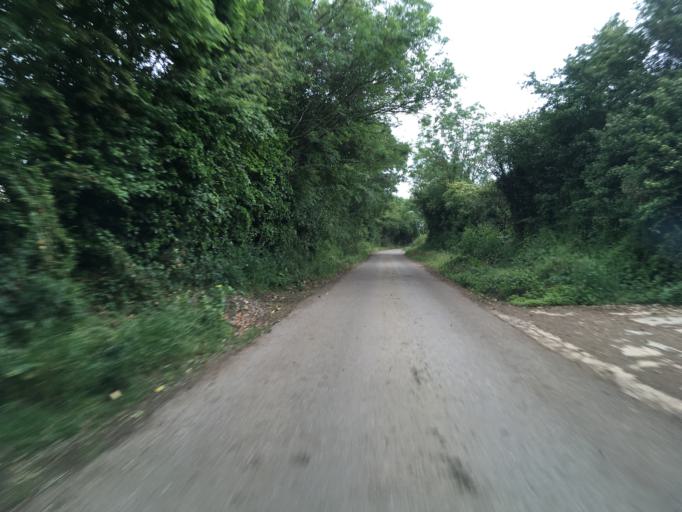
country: GB
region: England
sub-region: Wiltshire
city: Norton
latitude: 51.5909
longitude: -2.1725
